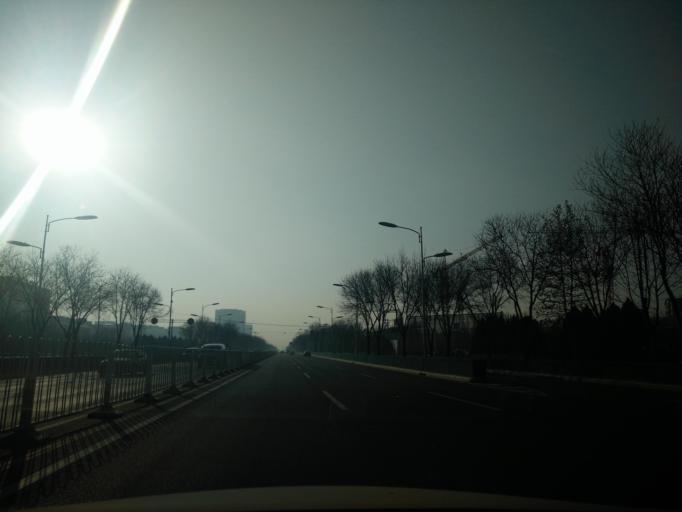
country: CN
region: Beijing
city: Jiugong
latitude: 39.7902
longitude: 116.5009
